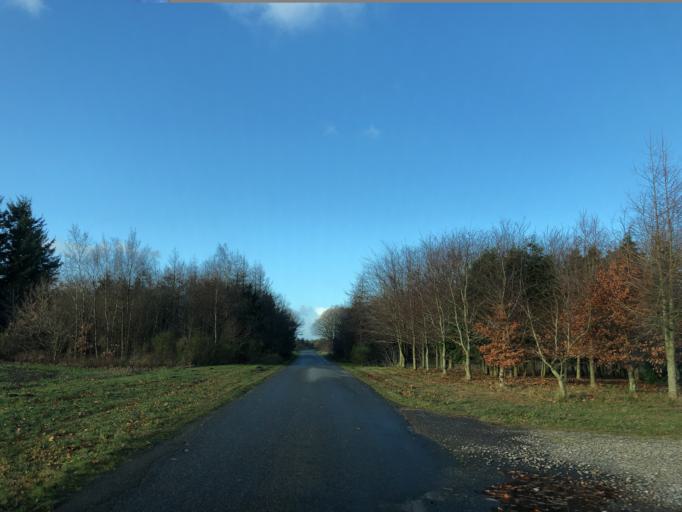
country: DK
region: Central Jutland
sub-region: Holstebro Kommune
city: Ulfborg
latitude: 56.2089
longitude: 8.2967
